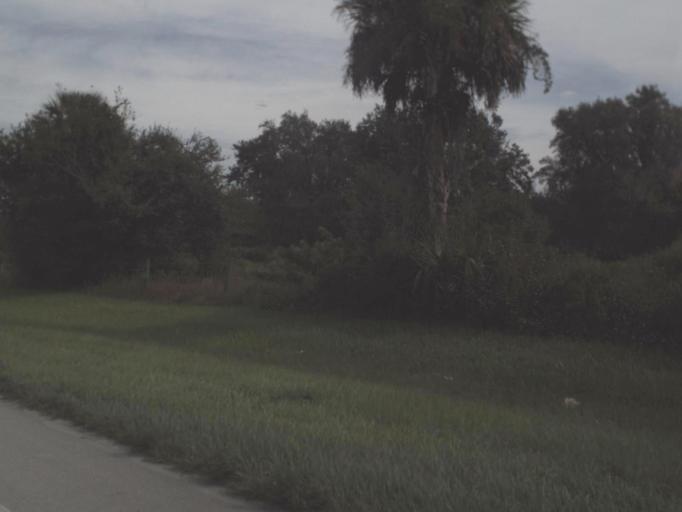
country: US
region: Florida
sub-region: DeSoto County
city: Southeast Arcadia
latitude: 27.1172
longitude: -81.7947
